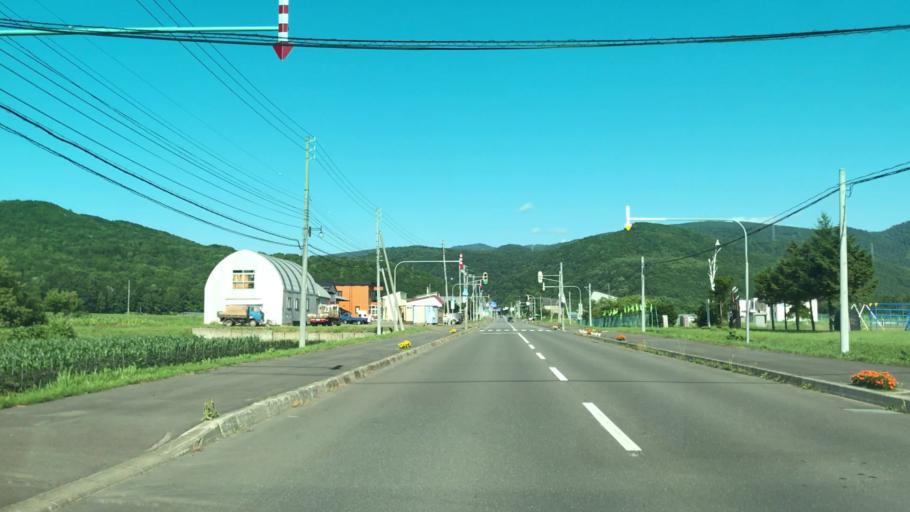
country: JP
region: Hokkaido
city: Yoichi
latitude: 43.0507
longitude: 140.8353
